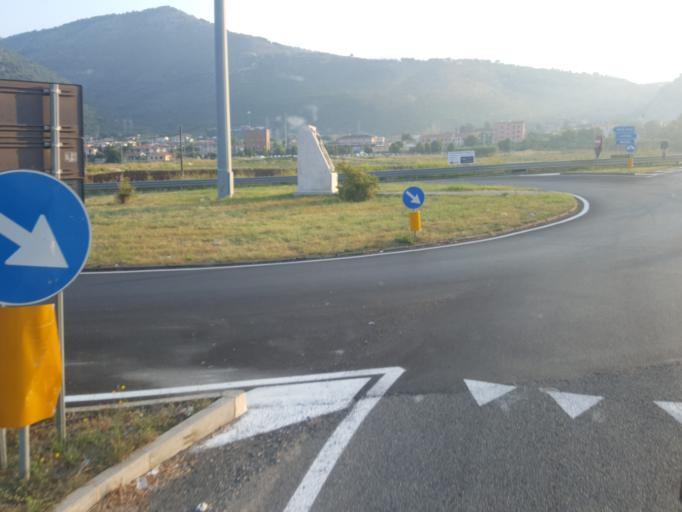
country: IT
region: Latium
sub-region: Provincia di Latina
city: Sezze Scalo
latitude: 41.4915
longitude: 13.0362
